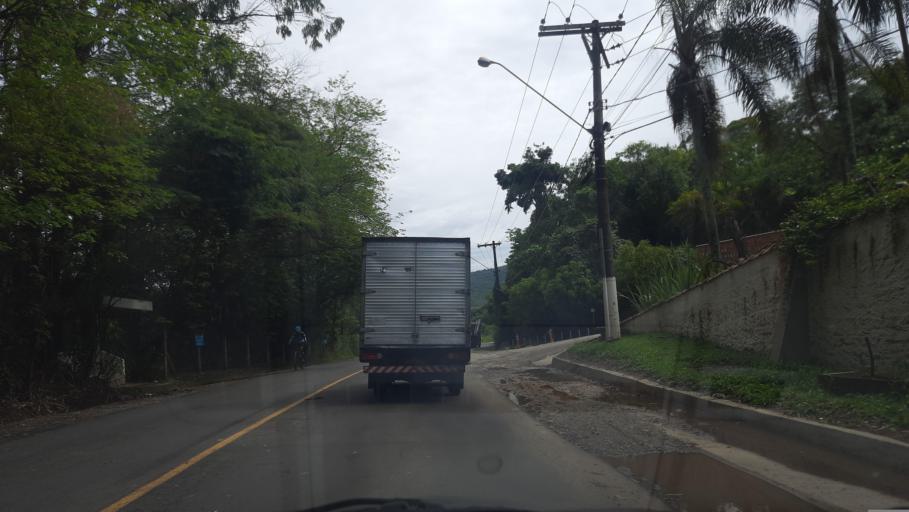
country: BR
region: Sao Paulo
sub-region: Franco Da Rocha
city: Franco da Rocha
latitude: -23.3476
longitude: -46.6637
